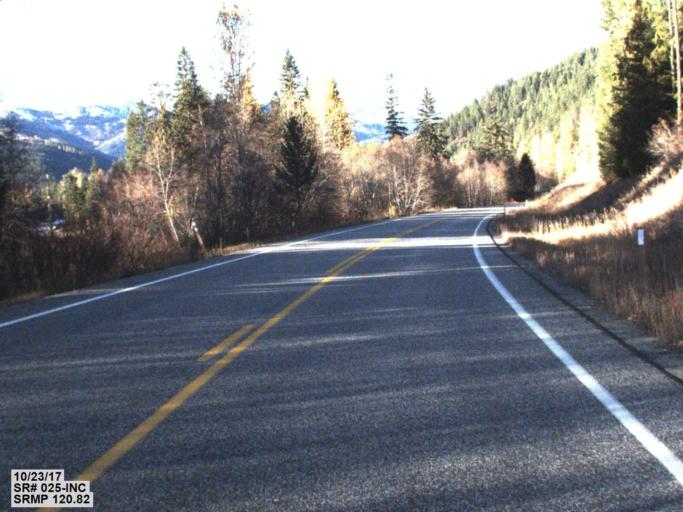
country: CA
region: British Columbia
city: Rossland
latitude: 48.9948
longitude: -117.8311
